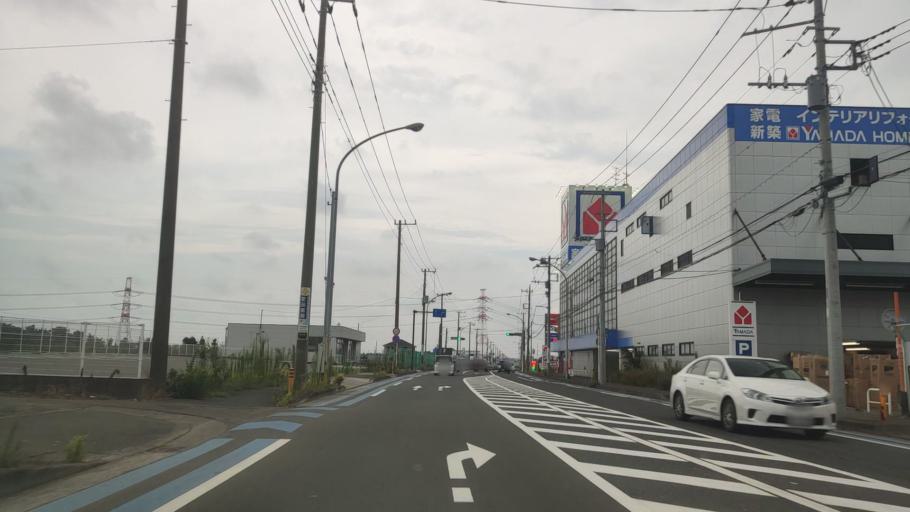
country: JP
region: Kanagawa
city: Minami-rinkan
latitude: 35.4354
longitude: 139.4847
